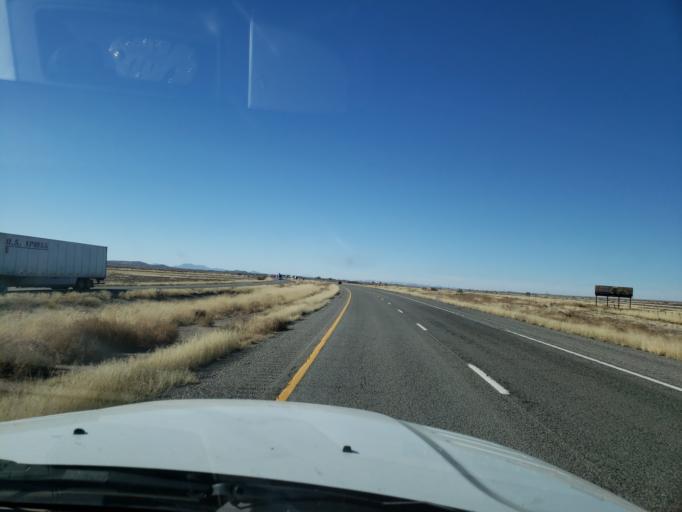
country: US
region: New Mexico
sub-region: Hidalgo County
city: Lordsburg
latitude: 32.3286
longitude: -108.6349
